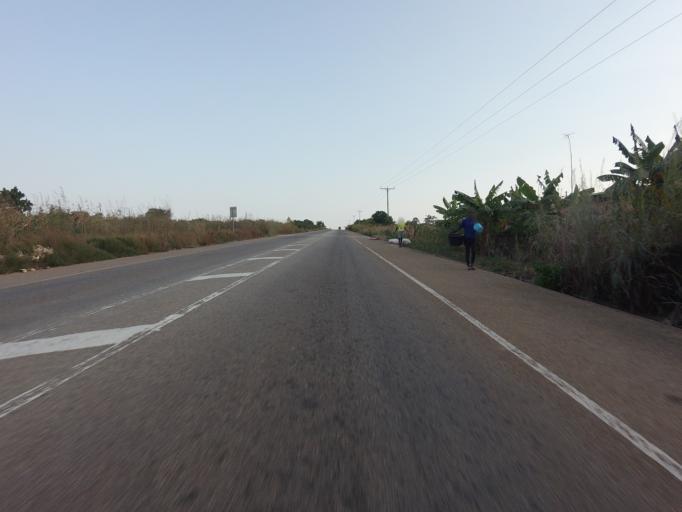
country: GH
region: Volta
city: Anloga
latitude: 6.0426
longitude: 0.6046
